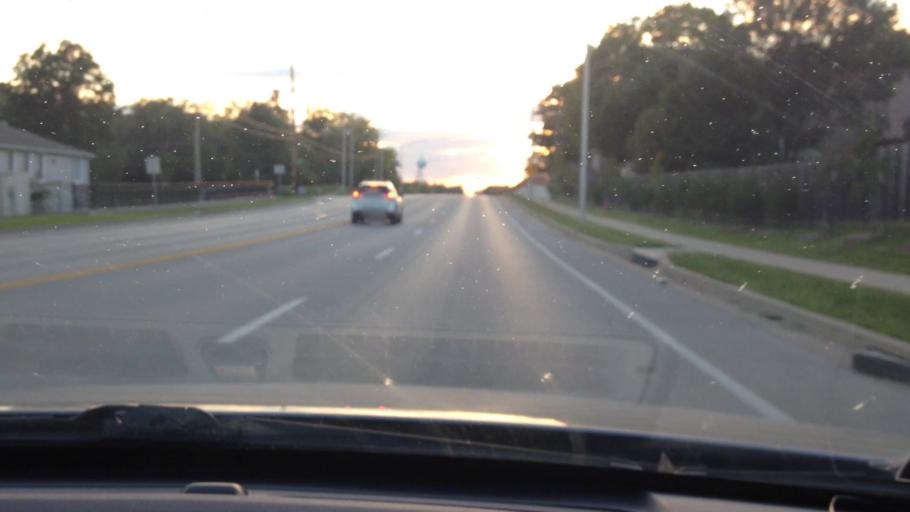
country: US
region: Missouri
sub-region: Platte County
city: Weatherby Lake
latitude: 39.2470
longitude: -94.6812
